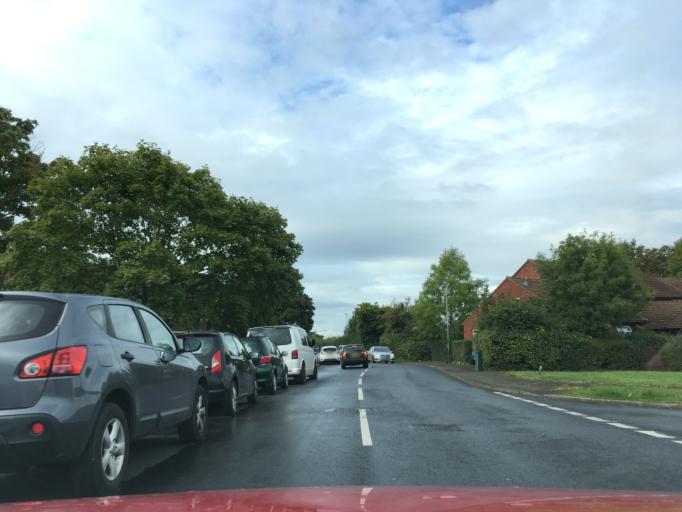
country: GB
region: England
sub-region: Gloucestershire
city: Uckington
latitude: 51.9023
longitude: -2.1263
